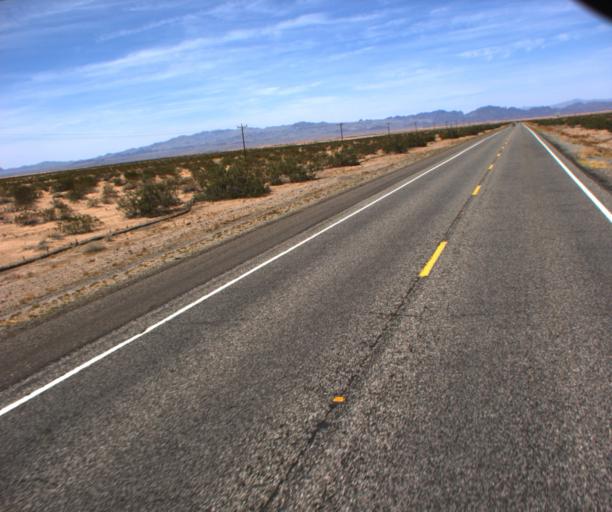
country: US
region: Arizona
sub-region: La Paz County
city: Parker
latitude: 34.0479
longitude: -114.2580
